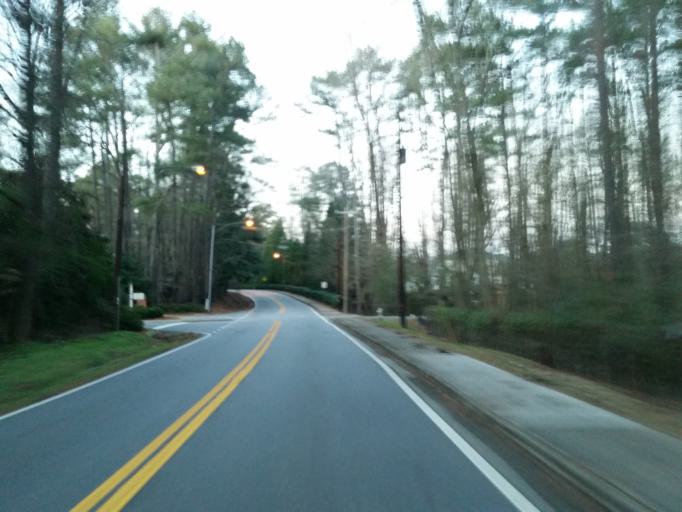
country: US
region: Georgia
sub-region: Cobb County
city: Vinings
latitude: 33.8558
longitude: -84.4612
